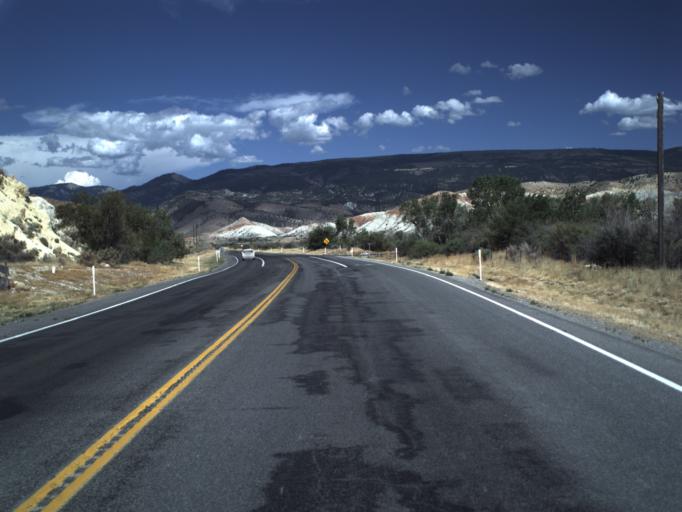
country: US
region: Utah
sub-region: Sanpete County
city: Gunnison
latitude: 39.1593
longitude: -111.7527
